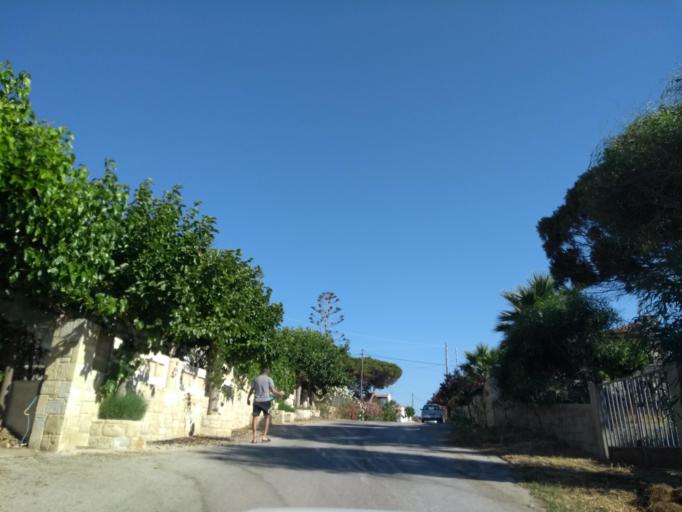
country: GR
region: Crete
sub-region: Nomos Chanias
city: Pithari
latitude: 35.5899
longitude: 24.0914
